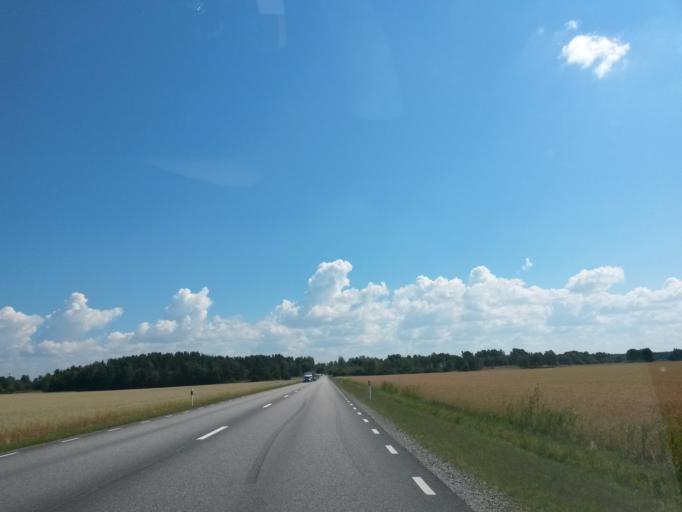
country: SE
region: Vaestra Goetaland
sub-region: Grastorps Kommun
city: Graestorp
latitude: 58.3250
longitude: 12.7368
